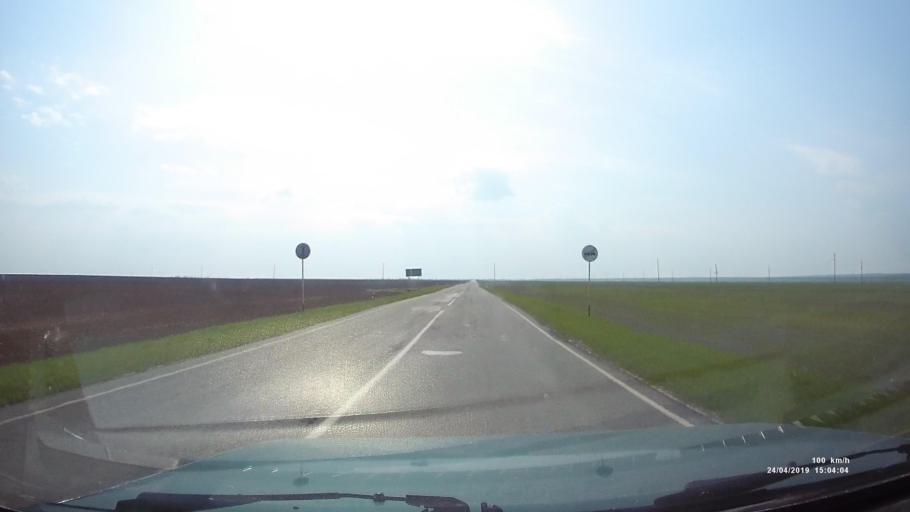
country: RU
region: Rostov
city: Remontnoye
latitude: 46.5633
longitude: 43.4784
